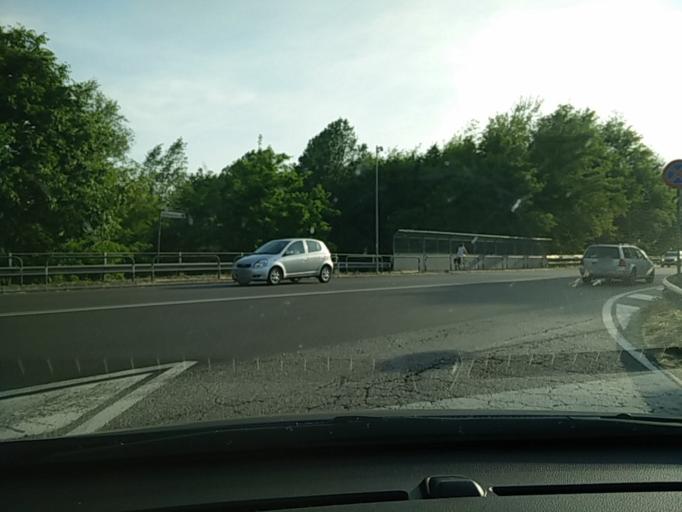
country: IT
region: Veneto
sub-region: Provincia di Padova
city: Padova
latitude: 45.4107
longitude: 11.8528
